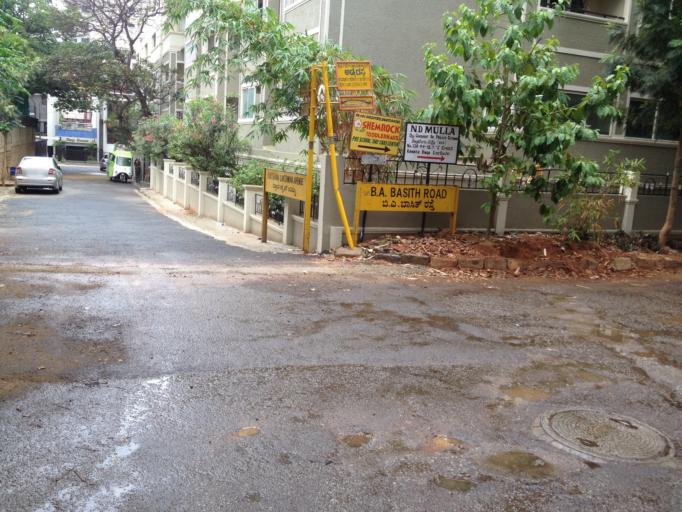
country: IN
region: Karnataka
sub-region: Bangalore Urban
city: Bangalore
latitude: 12.9909
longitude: 77.6604
